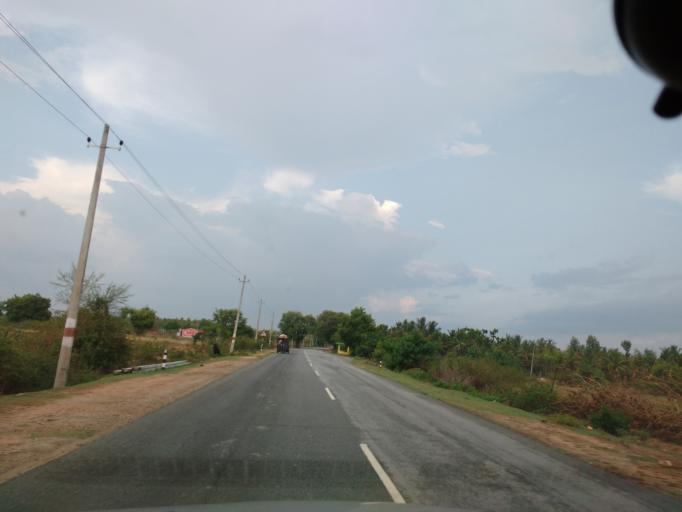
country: IN
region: Karnataka
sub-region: Hassan
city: Arsikere
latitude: 13.2951
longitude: 76.2997
